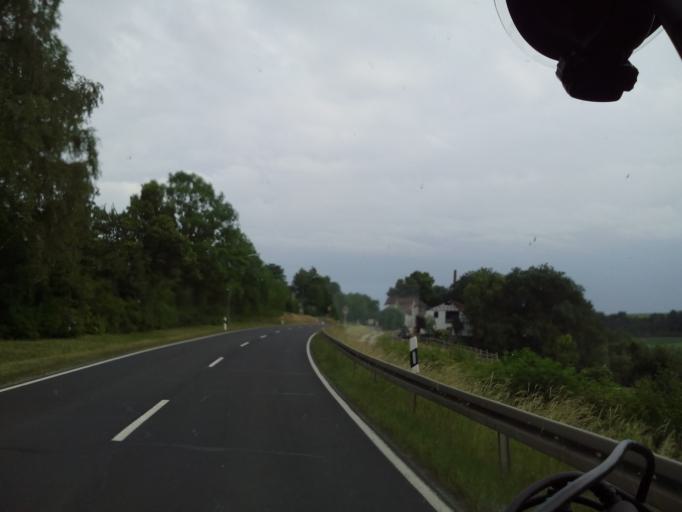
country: DE
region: Bavaria
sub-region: Regierungsbezirk Unterfranken
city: Stockheim
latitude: 50.4556
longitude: 10.2772
